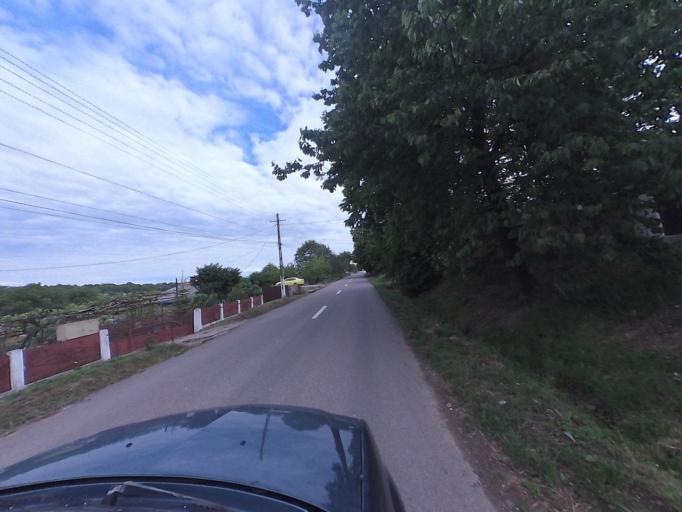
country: RO
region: Neamt
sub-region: Comuna Dulcesti
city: Dulcesti
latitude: 46.9606
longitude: 26.7861
